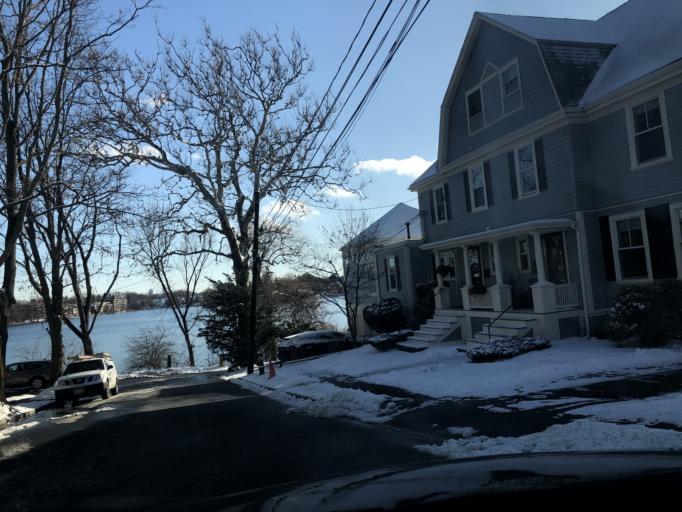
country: US
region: Massachusetts
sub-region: Middlesex County
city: Arlington
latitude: 42.4116
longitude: -71.1548
